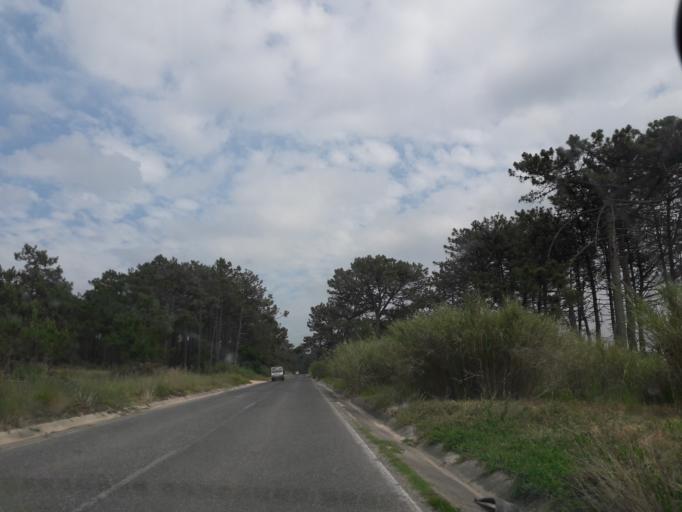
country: PT
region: Leiria
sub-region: Peniche
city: Atouguia da Baleia
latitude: 39.3587
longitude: -9.3020
